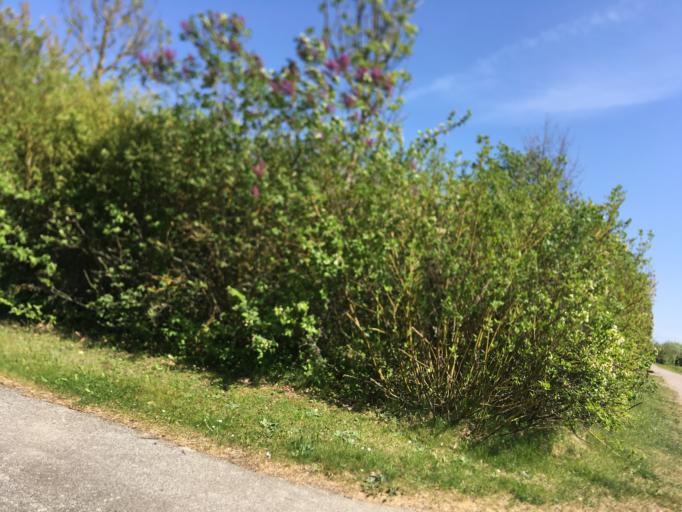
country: SE
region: Skane
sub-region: Staffanstorps Kommun
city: Hjaerup
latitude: 55.7019
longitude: 13.1544
